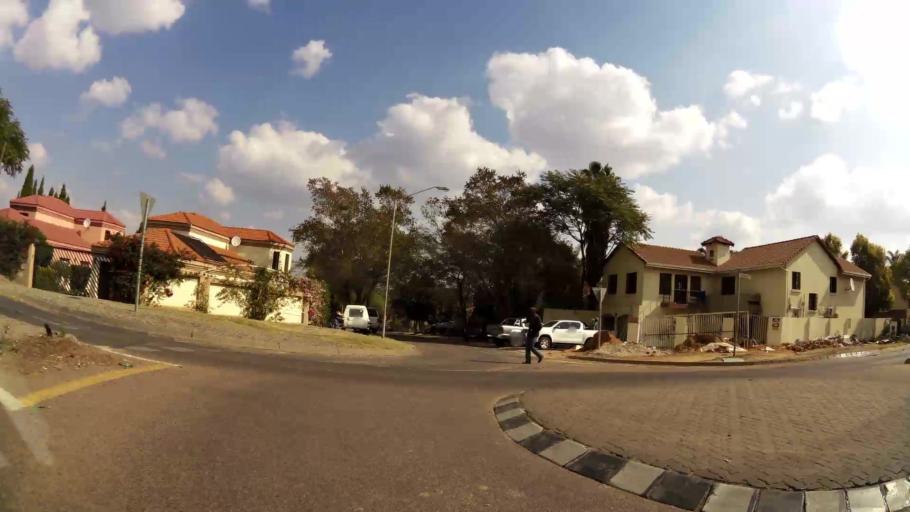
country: ZA
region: Gauteng
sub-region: City of Tshwane Metropolitan Municipality
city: Pretoria
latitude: -25.7963
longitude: 28.3308
